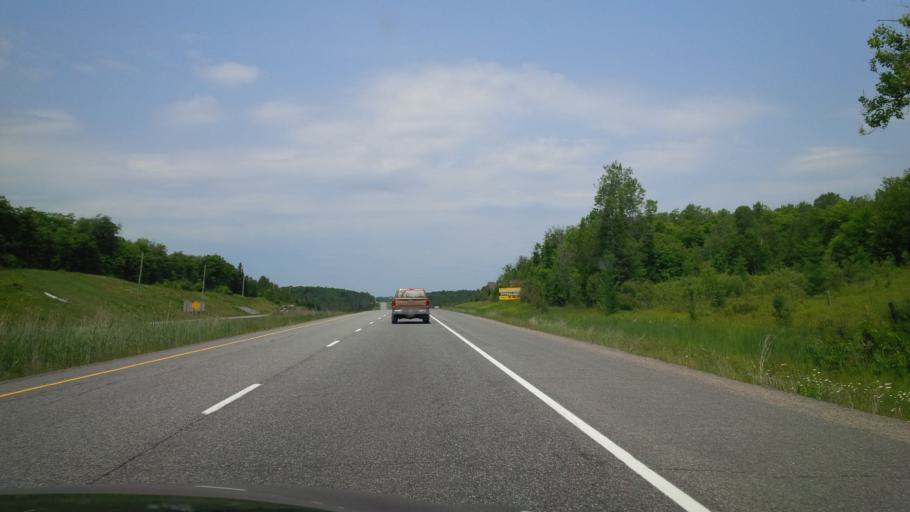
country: CA
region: Ontario
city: Huntsville
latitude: 45.4692
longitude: -79.2655
